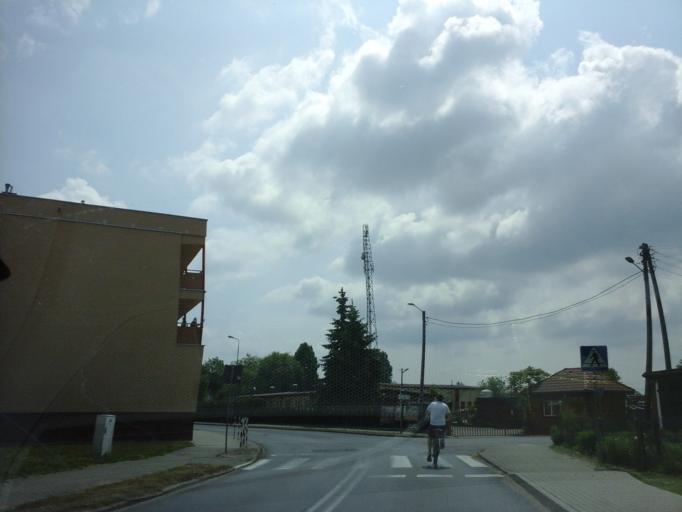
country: PL
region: West Pomeranian Voivodeship
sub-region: Powiat choszczenski
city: Drawno
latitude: 53.2161
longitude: 15.7647
